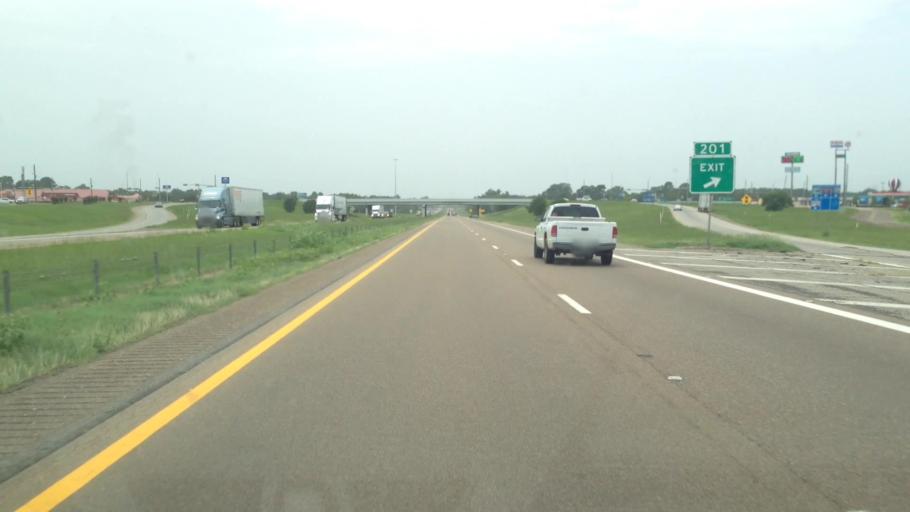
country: US
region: Texas
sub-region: Bowie County
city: New Boston
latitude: 33.4742
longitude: -94.4053
